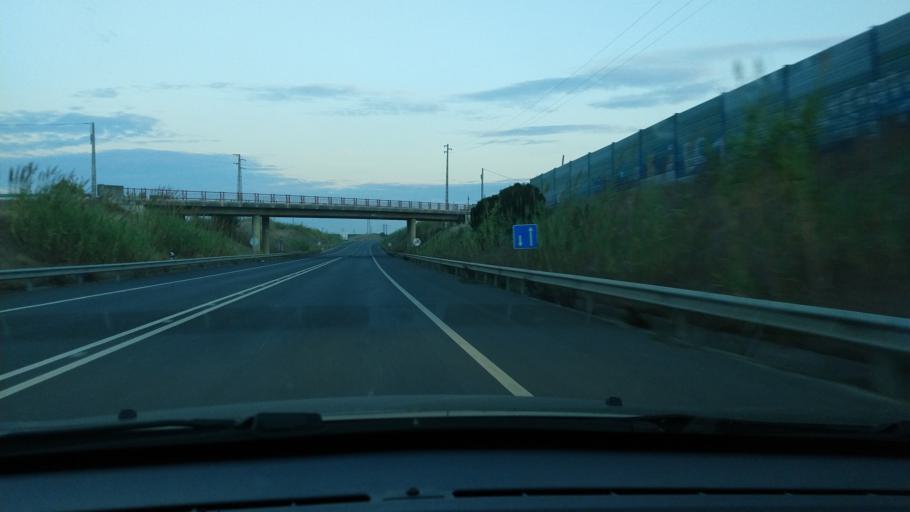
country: PT
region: Leiria
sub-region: Peniche
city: Atouguia da Baleia
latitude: 39.3293
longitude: -9.3241
